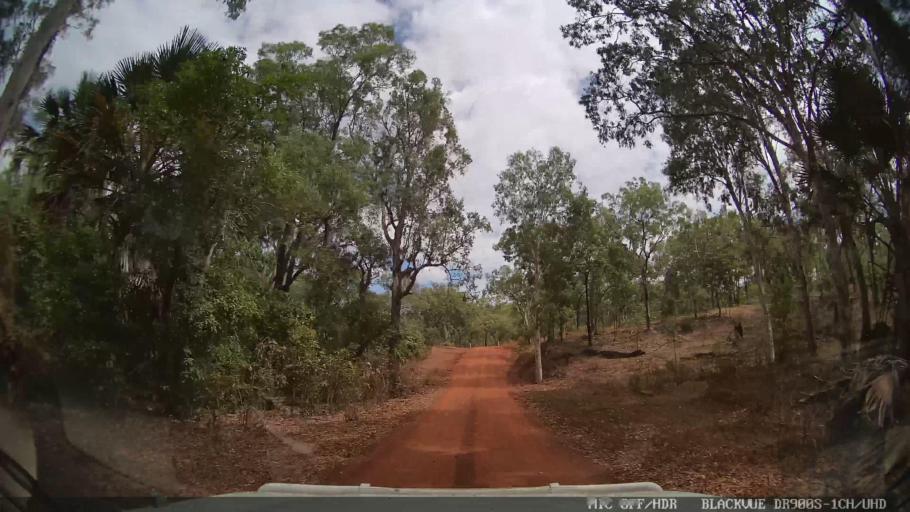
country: AU
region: Queensland
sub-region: Cook
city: Cooktown
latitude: -15.2923
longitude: 144.8435
